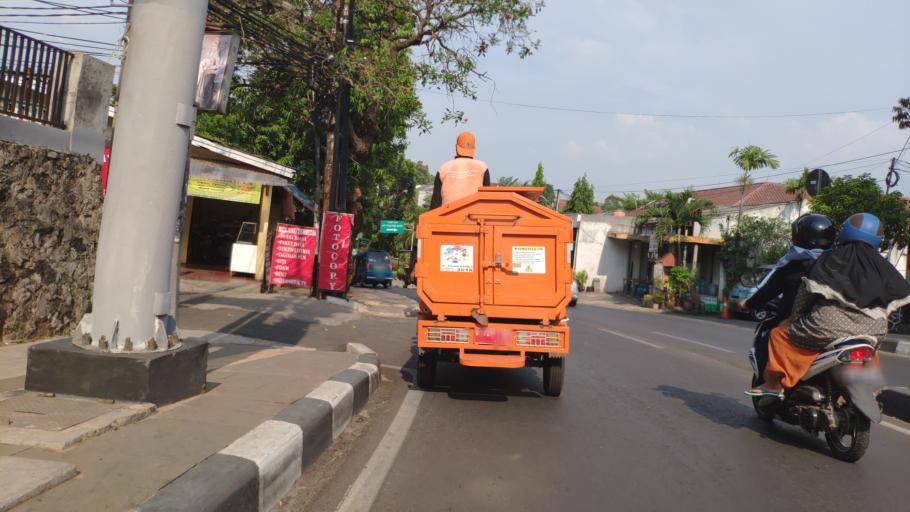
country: ID
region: Jakarta Raya
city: Jakarta
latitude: -6.2861
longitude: 106.8343
